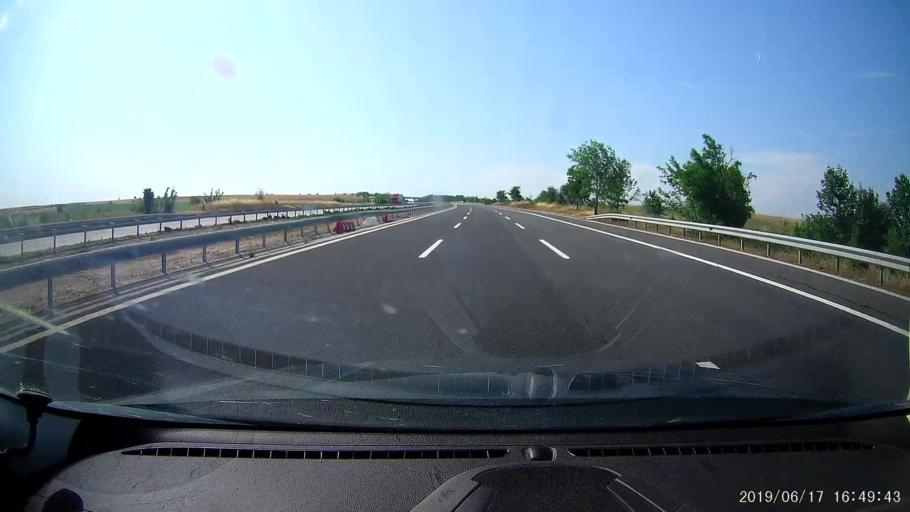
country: TR
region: Kirklareli
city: Babaeski
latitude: 41.5134
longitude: 27.1074
